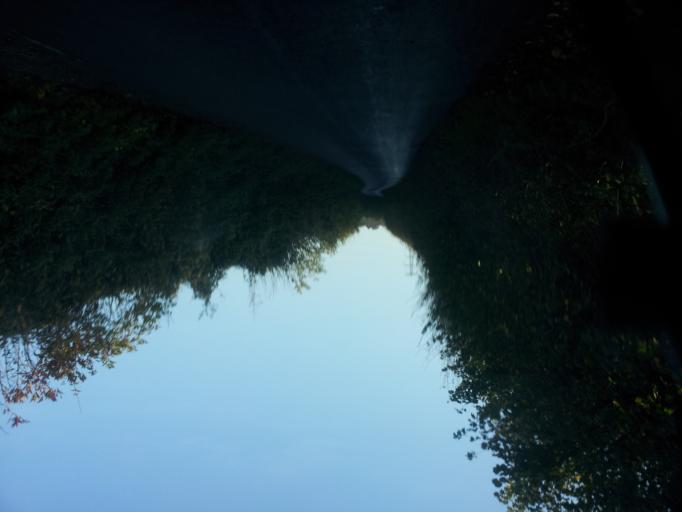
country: GB
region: England
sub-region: Kent
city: Harrietsham
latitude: 51.2825
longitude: 0.6200
